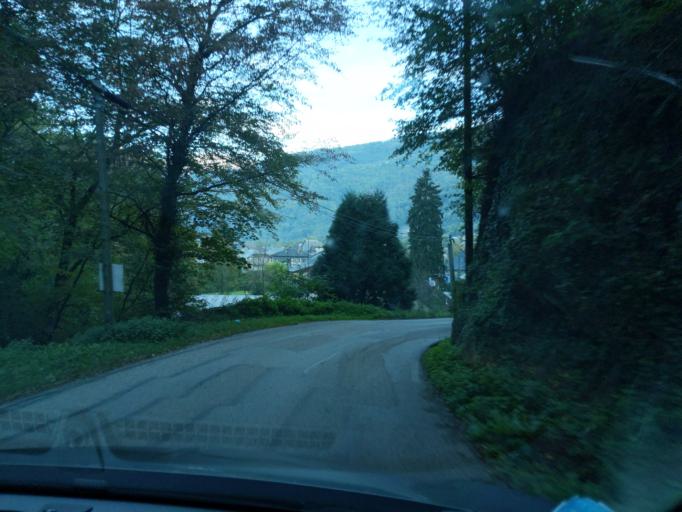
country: FR
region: Rhone-Alpes
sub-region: Departement de la Savoie
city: Aiton
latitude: 45.5392
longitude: 6.3083
